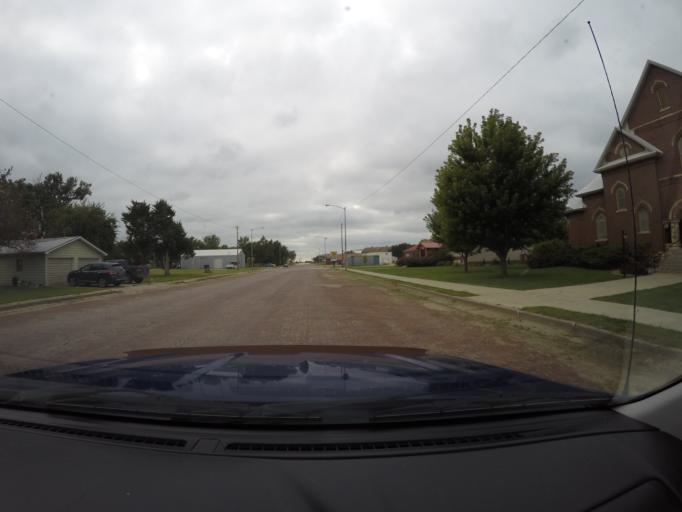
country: US
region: Kansas
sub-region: Geary County
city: Grandview Plaza
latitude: 38.7957
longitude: -96.7376
